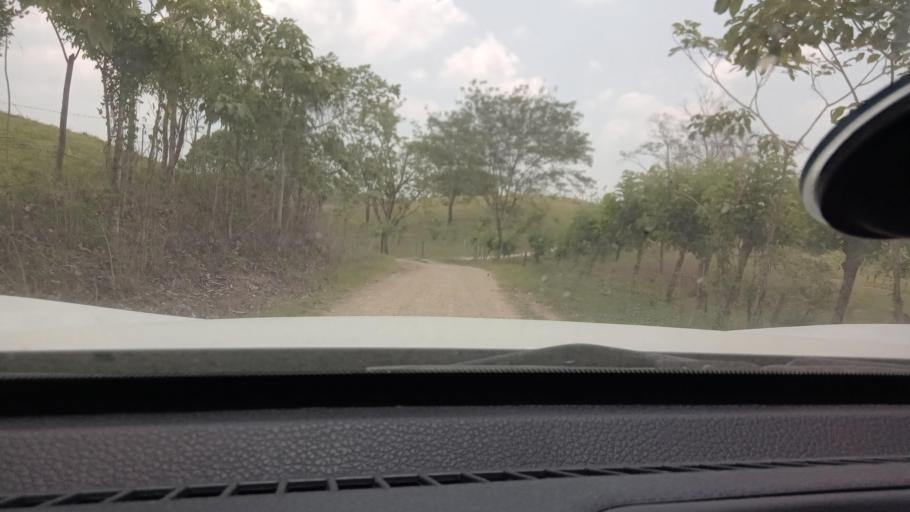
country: MX
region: Tabasco
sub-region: Huimanguillo
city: Francisco Rueda
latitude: 17.4951
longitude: -93.9300
